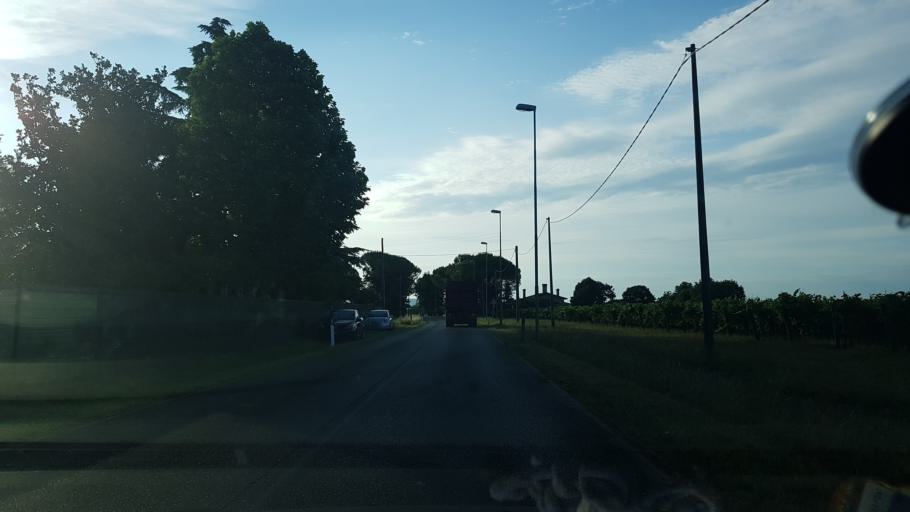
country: IT
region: Friuli Venezia Giulia
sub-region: Provincia di Udine
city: Chiopris
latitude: 45.9237
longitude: 13.3855
